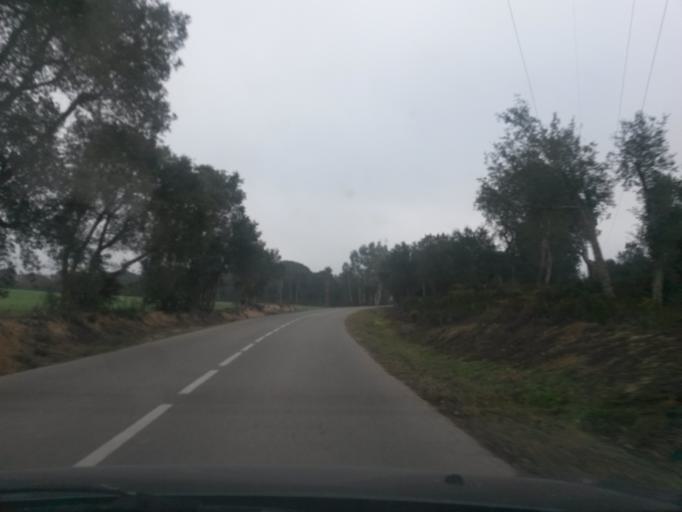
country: ES
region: Catalonia
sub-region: Provincia de Girona
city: Llagostera
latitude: 41.8381
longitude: 2.9416
